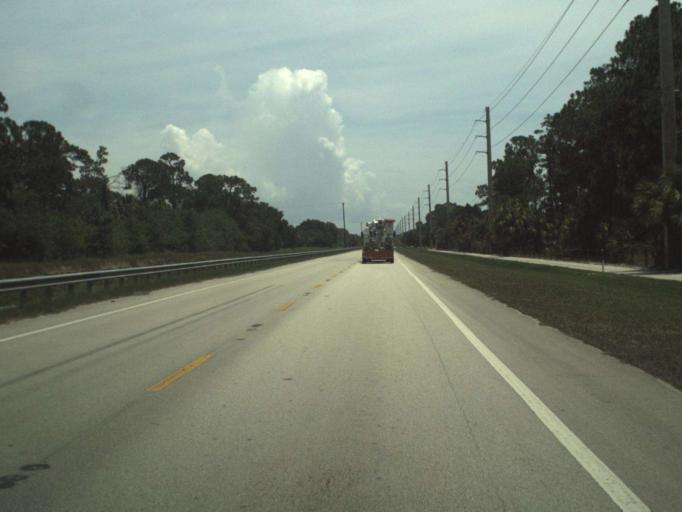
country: US
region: Florida
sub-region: Saint Lucie County
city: Lakewood Park
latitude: 27.5370
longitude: -80.4147
